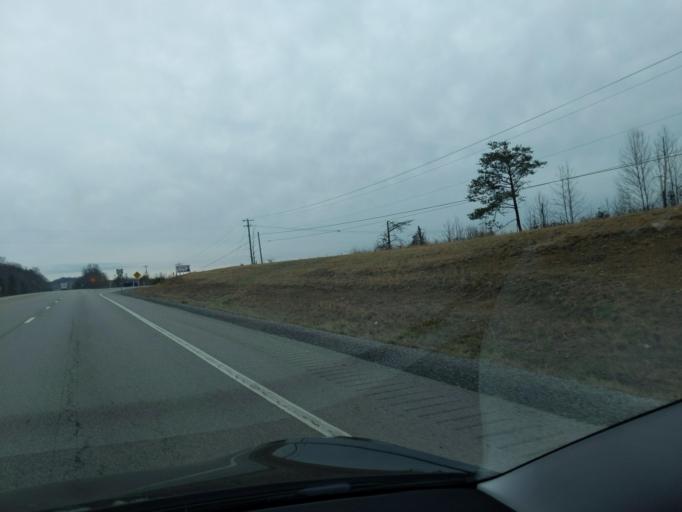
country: US
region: Kentucky
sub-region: Whitley County
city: Corbin
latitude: 36.9150
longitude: -84.0755
